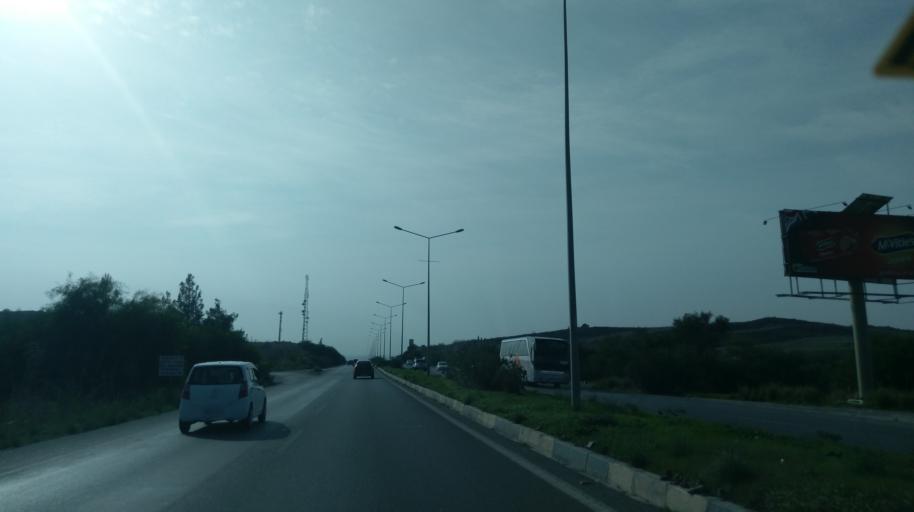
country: CY
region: Lefkosia
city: Nicosia
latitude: 35.2356
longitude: 33.3117
